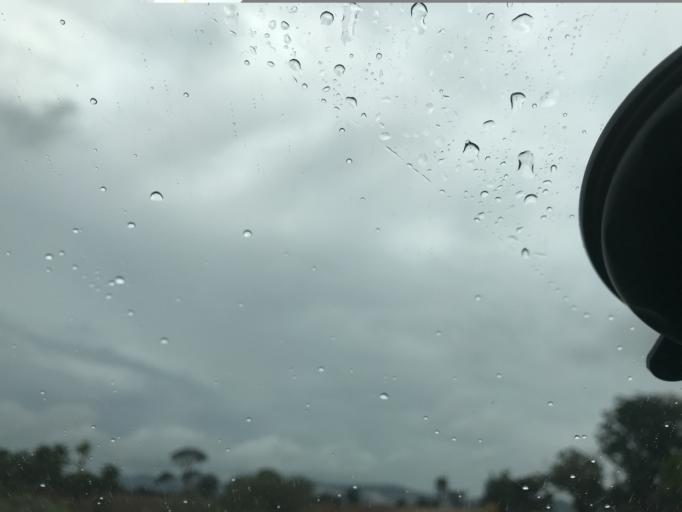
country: BR
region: Minas Gerais
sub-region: Conceicao Do Rio Verde
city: Conceicao do Rio Verde
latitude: -21.6889
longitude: -45.0102
